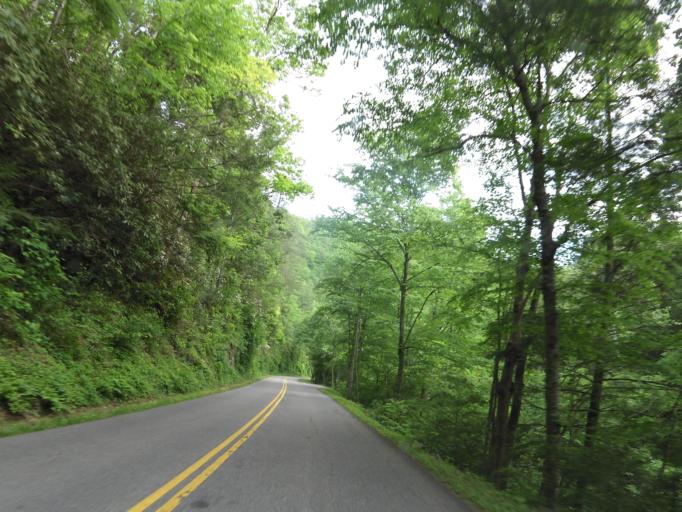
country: US
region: Tennessee
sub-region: Sevier County
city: Gatlinburg
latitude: 35.6686
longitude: -83.6284
